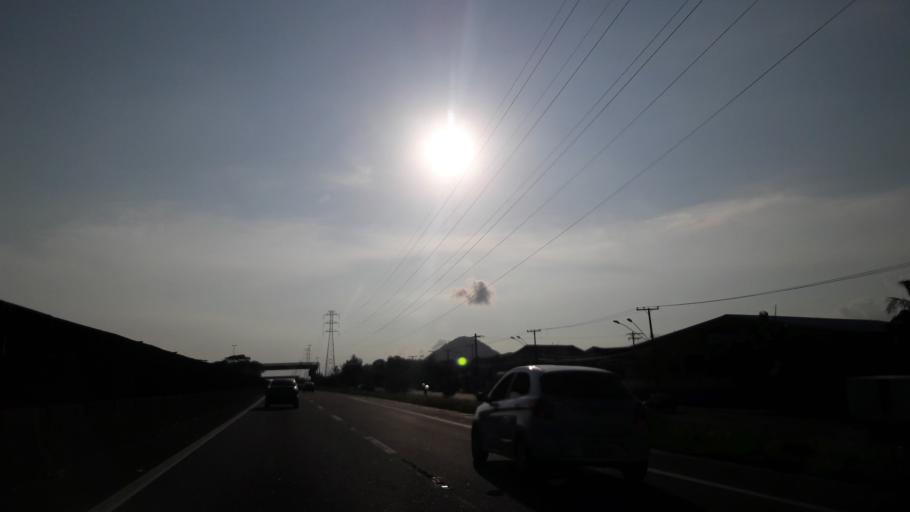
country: BR
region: Sao Paulo
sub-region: Mongagua
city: Mongagua
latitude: -24.1080
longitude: -46.6504
